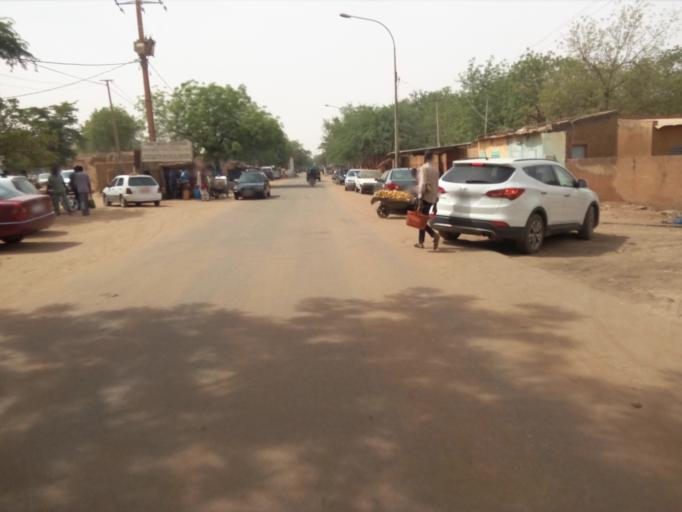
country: NE
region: Niamey
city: Niamey
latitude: 13.5189
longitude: 2.1117
